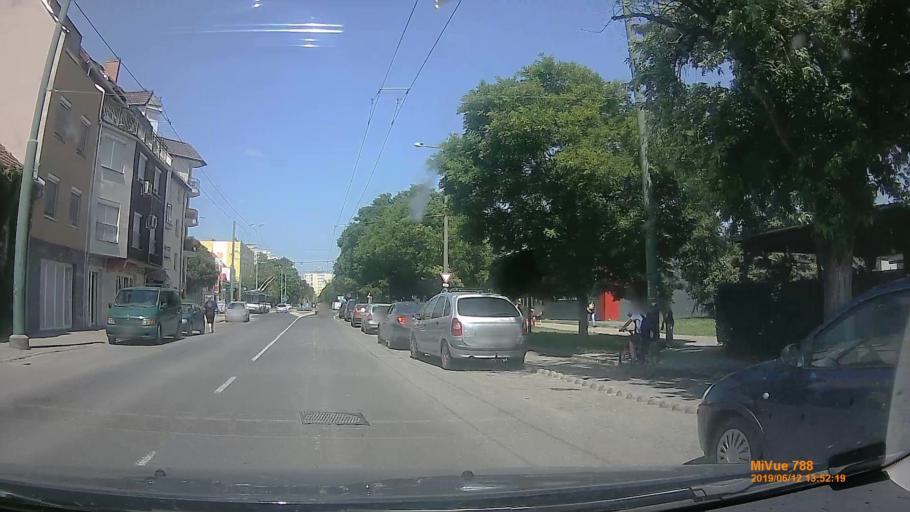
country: HU
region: Csongrad
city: Szeged
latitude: 46.2628
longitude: 20.1637
